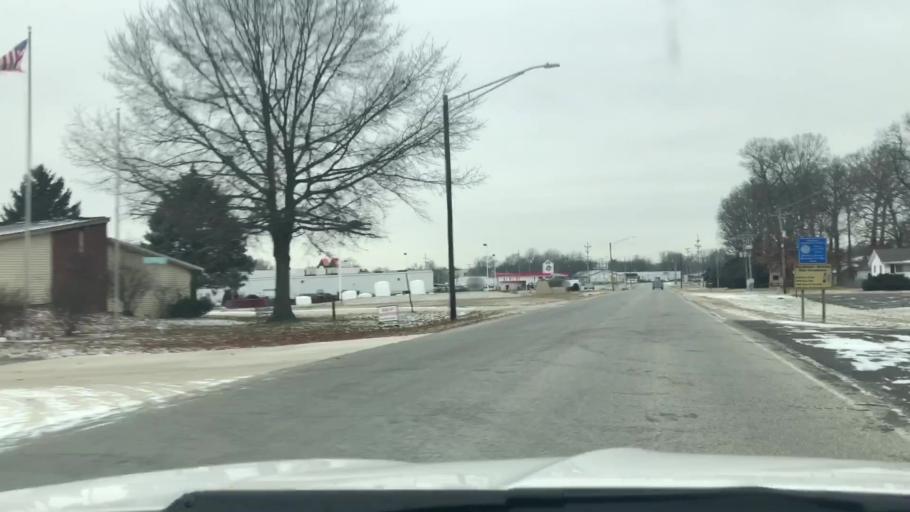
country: US
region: Indiana
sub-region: Fulton County
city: Rochester
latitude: 41.0529
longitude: -86.2137
